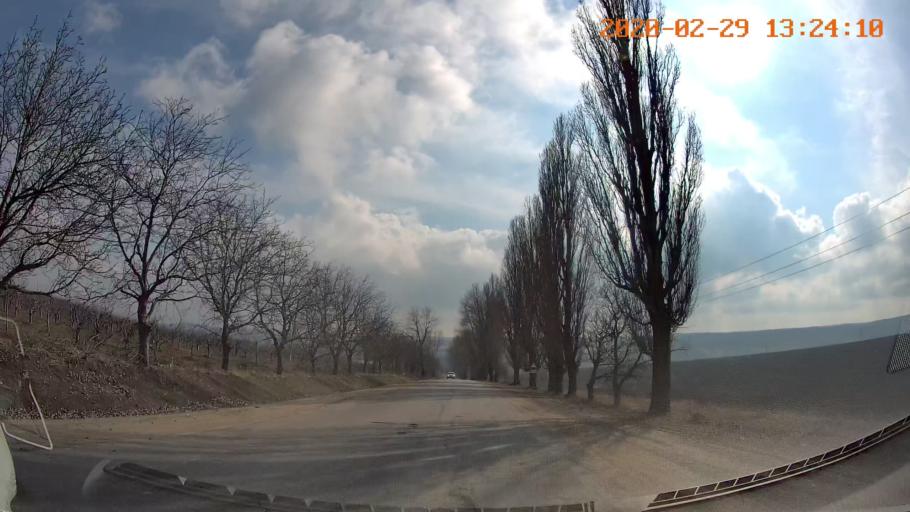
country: MD
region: Telenesti
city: Camenca
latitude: 47.9417
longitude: 28.6262
